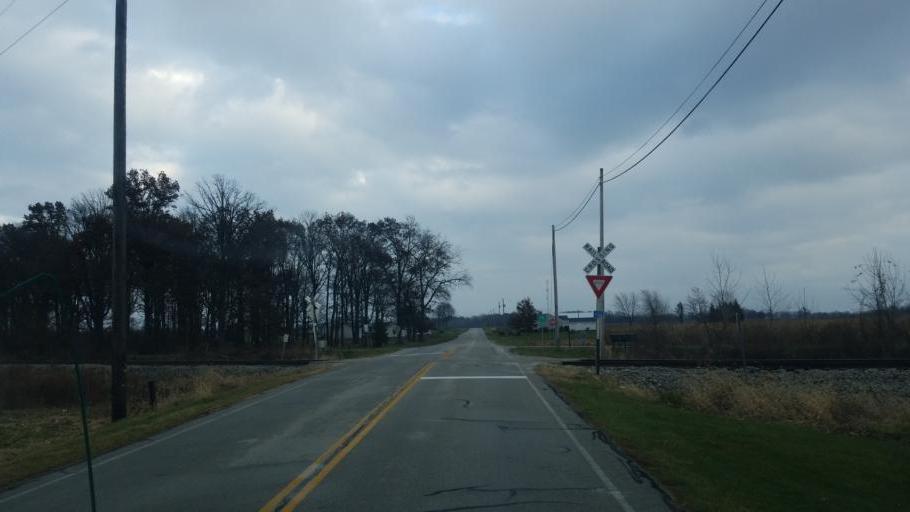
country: US
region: Ohio
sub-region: Mercer County
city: Coldwater
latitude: 40.5091
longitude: -84.6028
